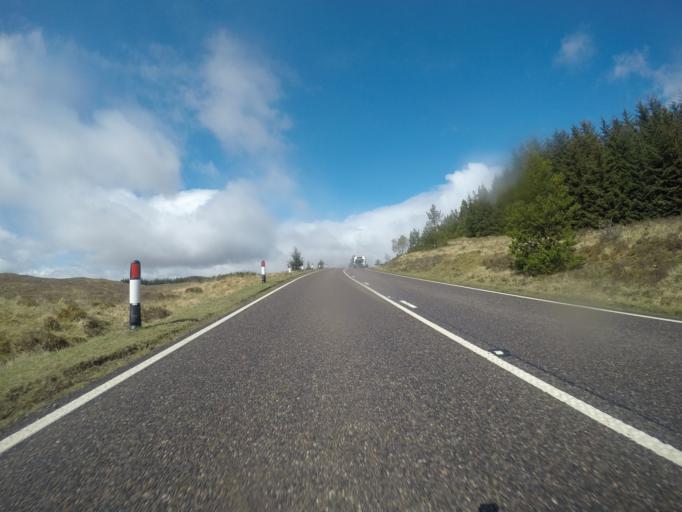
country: GB
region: Scotland
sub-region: Highland
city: Spean Bridge
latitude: 57.0936
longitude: -4.9906
